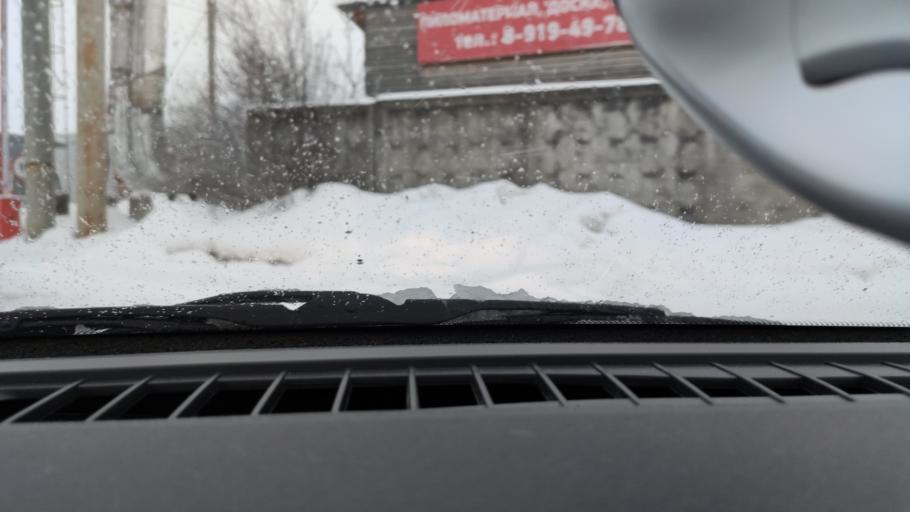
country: RU
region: Perm
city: Kondratovo
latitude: 57.9985
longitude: 56.1064
